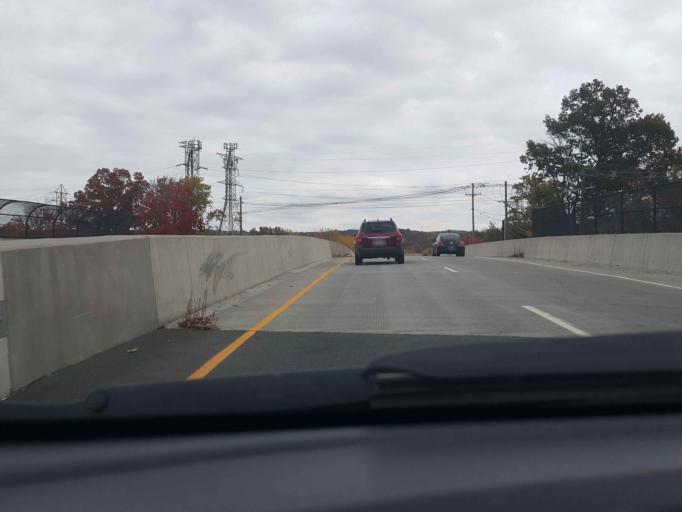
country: US
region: New York
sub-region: Rockland County
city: West Nyack
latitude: 41.0932
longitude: -73.9653
